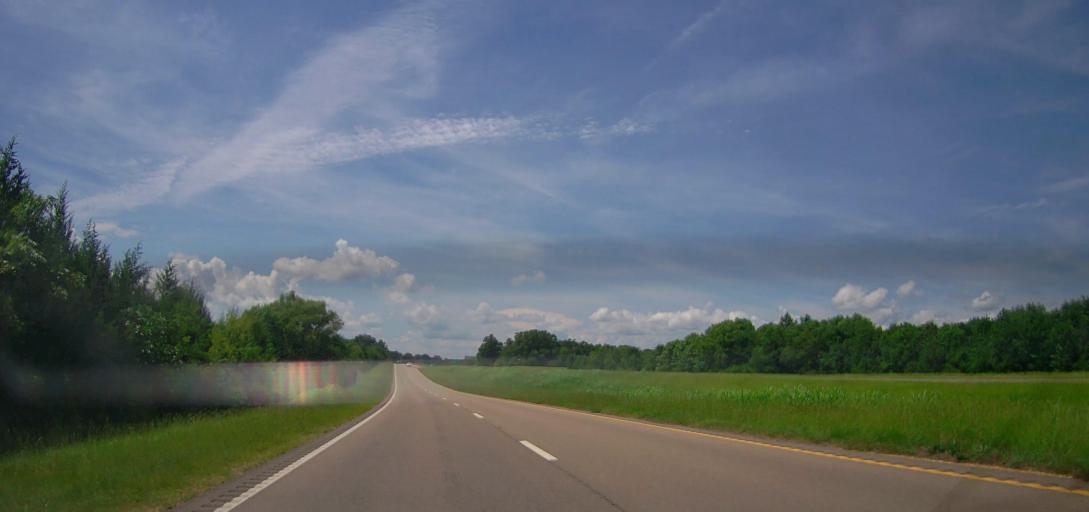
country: US
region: Mississippi
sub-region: Monroe County
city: Amory
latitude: 33.9540
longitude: -88.6055
